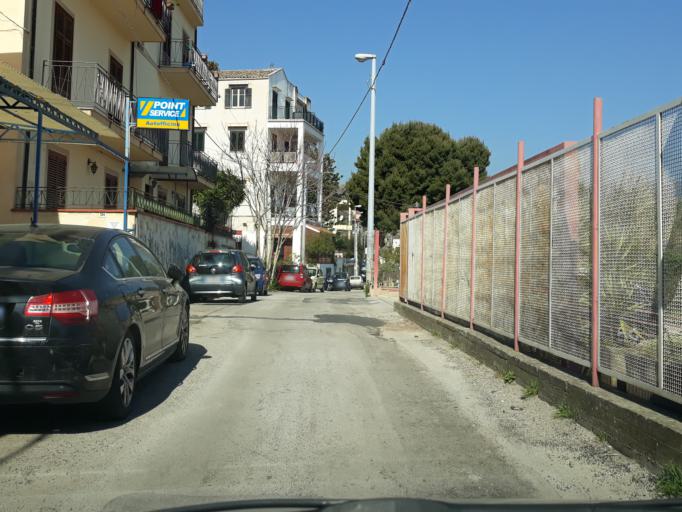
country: IT
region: Sicily
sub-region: Palermo
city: Piano dei Geli
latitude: 38.1098
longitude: 13.3006
